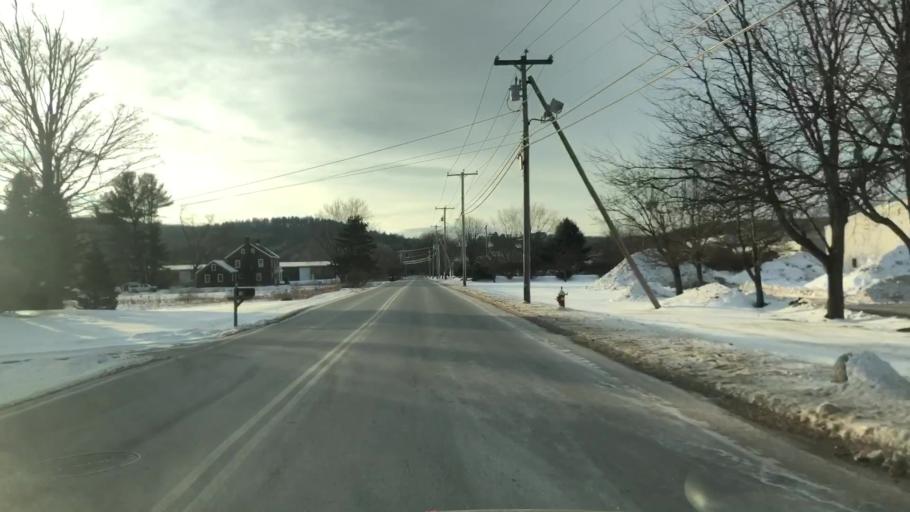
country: US
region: New Hampshire
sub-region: Hillsborough County
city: Wilton
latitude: 42.8393
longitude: -71.6943
